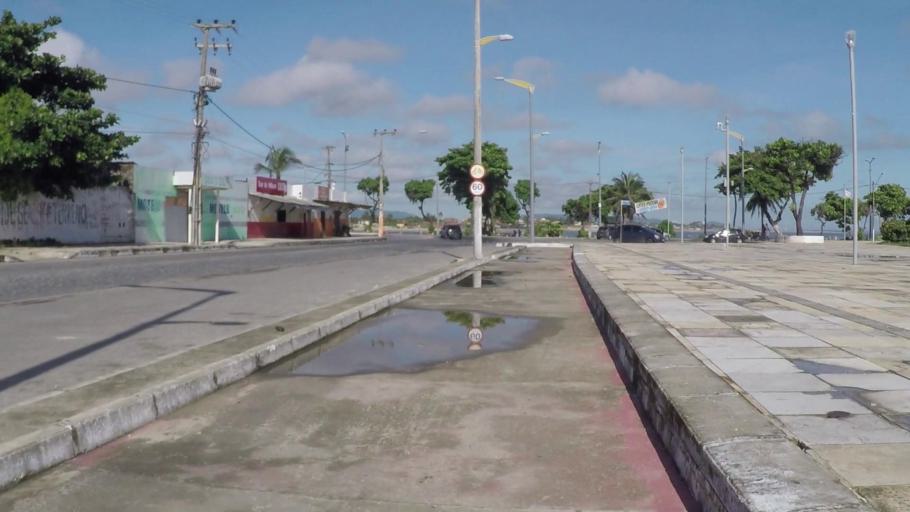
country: BR
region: Ceara
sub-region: Fortaleza
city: Fortaleza
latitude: -3.6943
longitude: -38.5857
